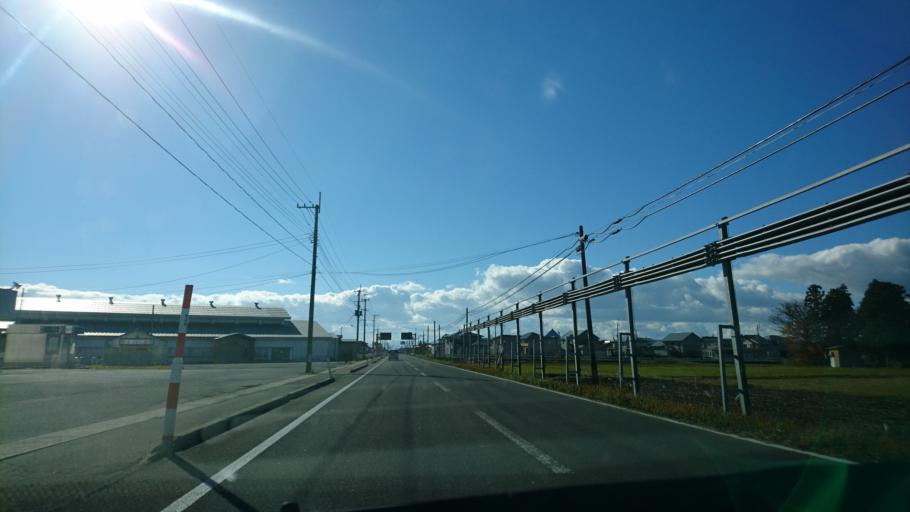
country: JP
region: Akita
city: Yokotemachi
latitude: 39.2861
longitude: 140.5193
